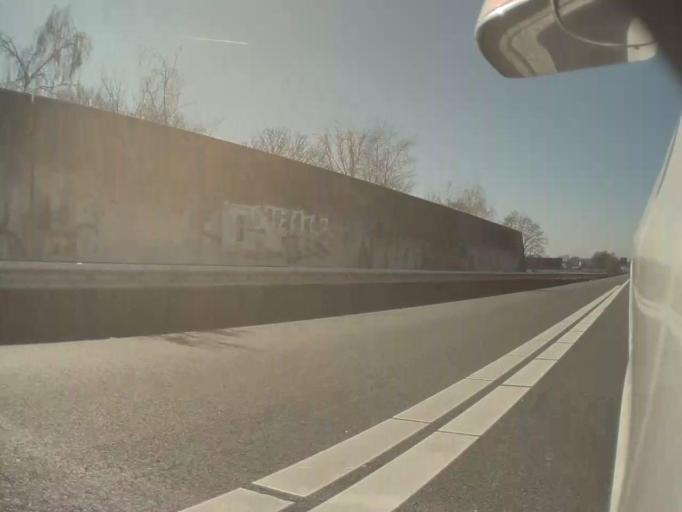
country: NL
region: North Brabant
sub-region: Gemeente Bernheze
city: Heesch
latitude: 51.7371
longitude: 5.5047
